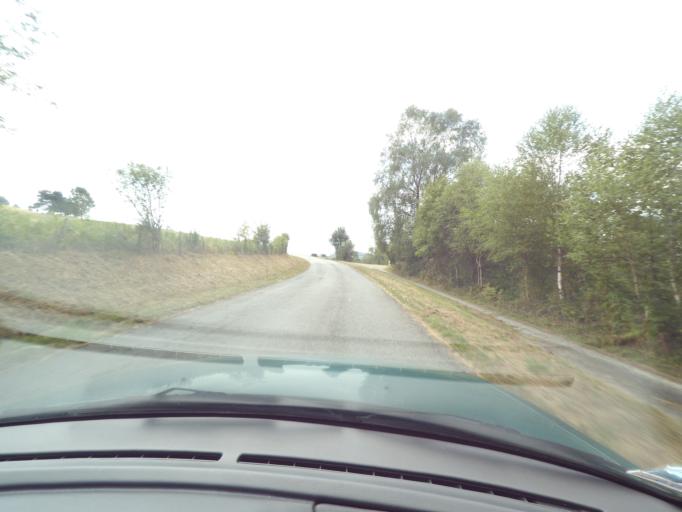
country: FR
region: Limousin
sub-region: Departement de la Correze
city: Bugeat
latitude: 45.7292
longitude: 1.9963
